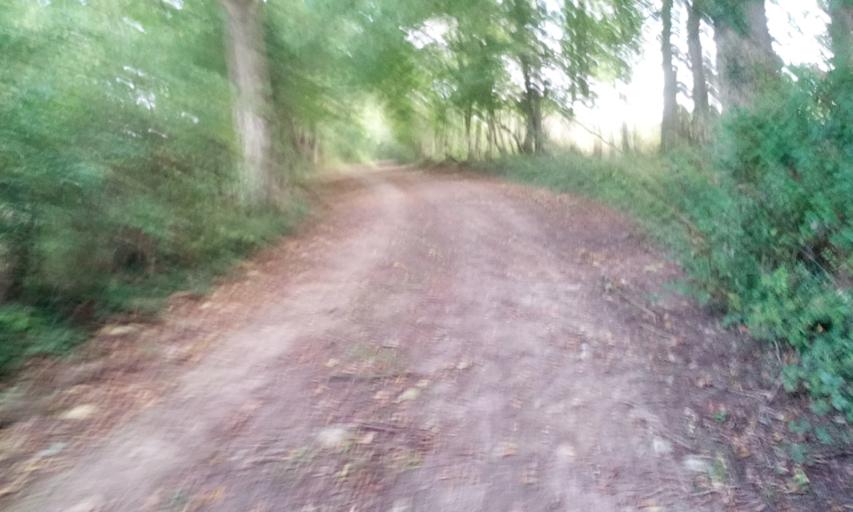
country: FR
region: Lower Normandy
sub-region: Departement du Calvados
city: Argences
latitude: 49.1267
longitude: -0.1388
